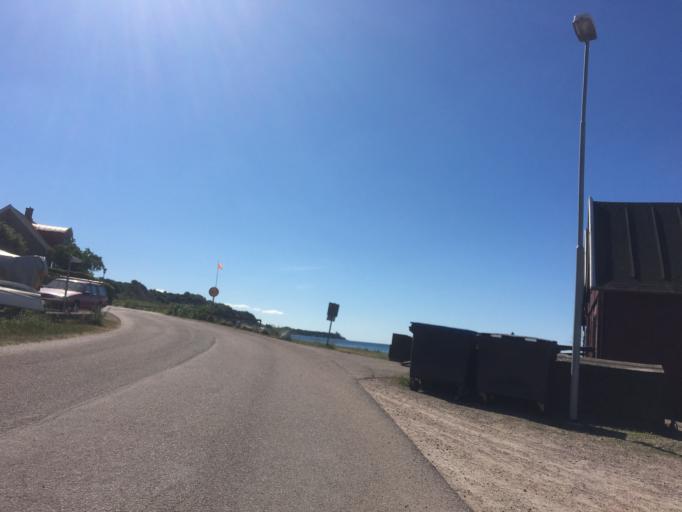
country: SE
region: Skane
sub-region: Helsingborg
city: Rydeback
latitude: 55.9097
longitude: 12.6747
